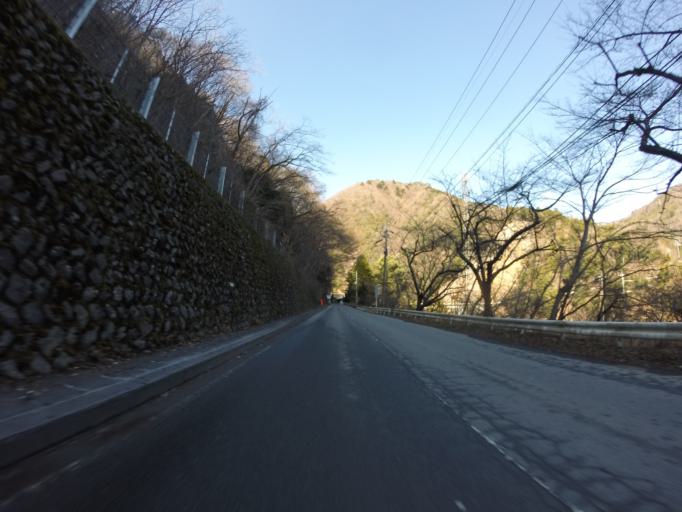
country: JP
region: Yamanashi
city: Ryuo
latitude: 35.4107
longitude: 138.3648
